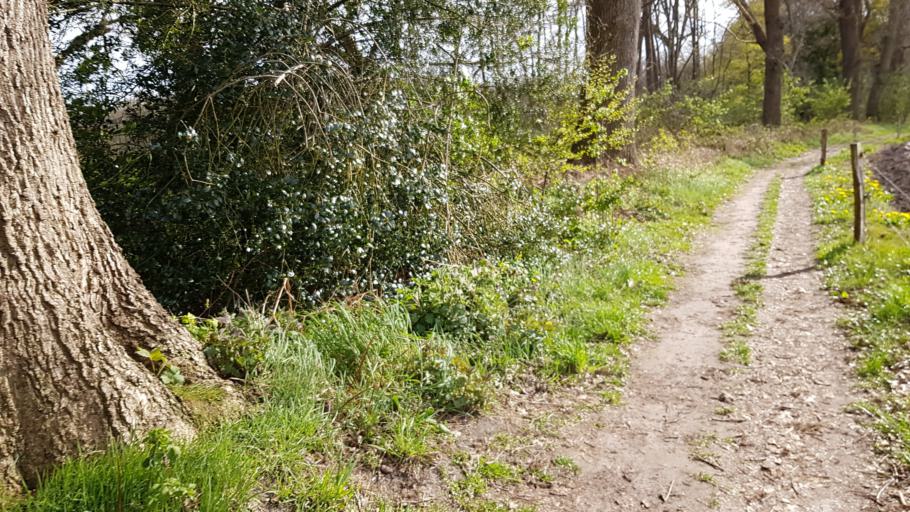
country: NL
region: Gelderland
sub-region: Gemeente Barneveld
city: Terschuur
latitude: 52.1850
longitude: 5.5497
